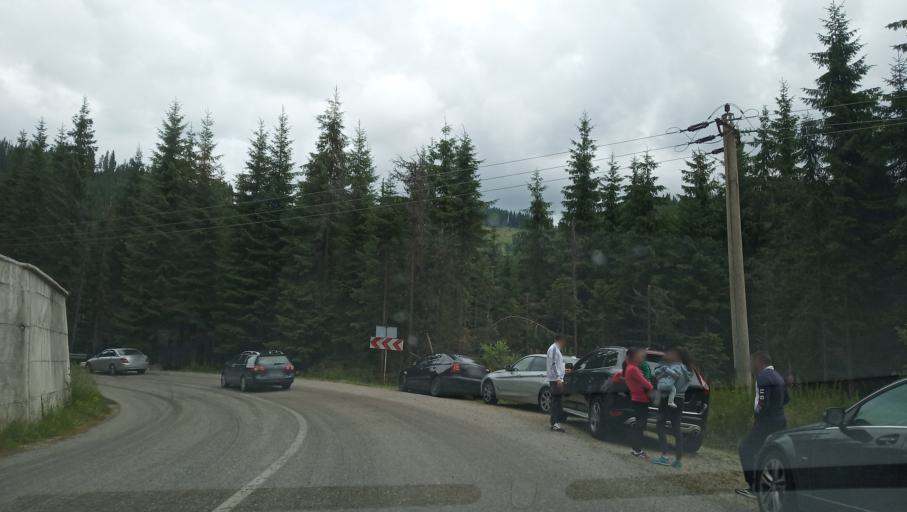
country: RO
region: Gorj
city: Novaci-Straini
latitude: 45.4294
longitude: 23.6787
